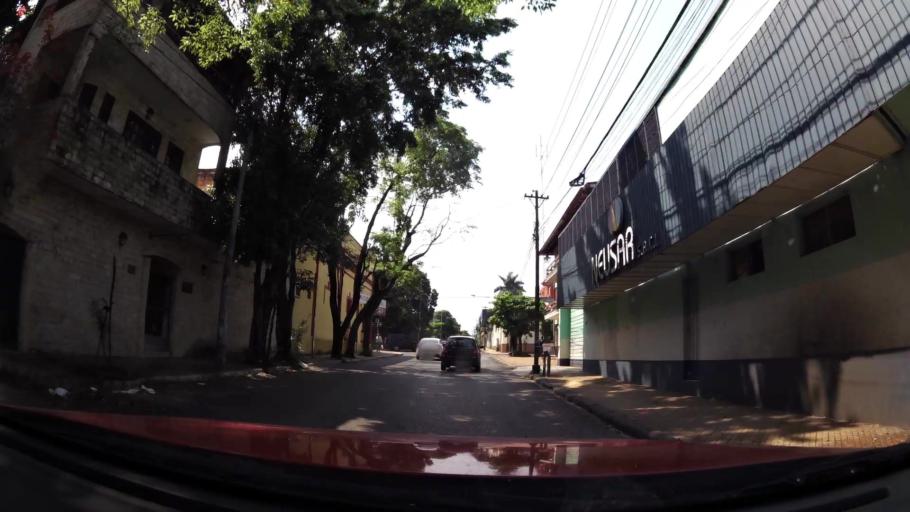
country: PY
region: Asuncion
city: Asuncion
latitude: -25.2926
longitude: -57.6399
